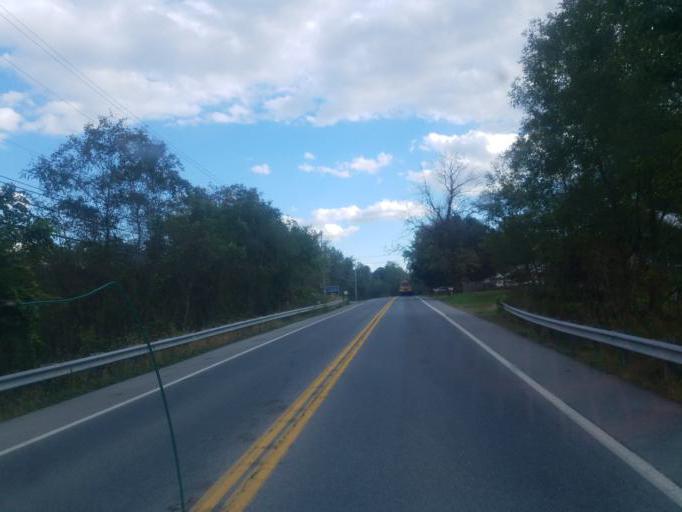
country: US
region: Pennsylvania
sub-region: Dauphin County
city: Middletown
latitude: 40.1688
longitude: -76.7217
